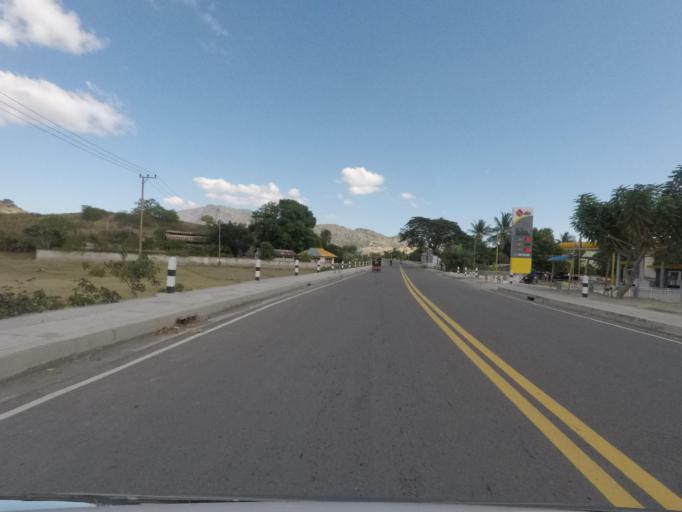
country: TL
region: Manatuto
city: Manatuto
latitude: -8.5179
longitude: 126.0050
